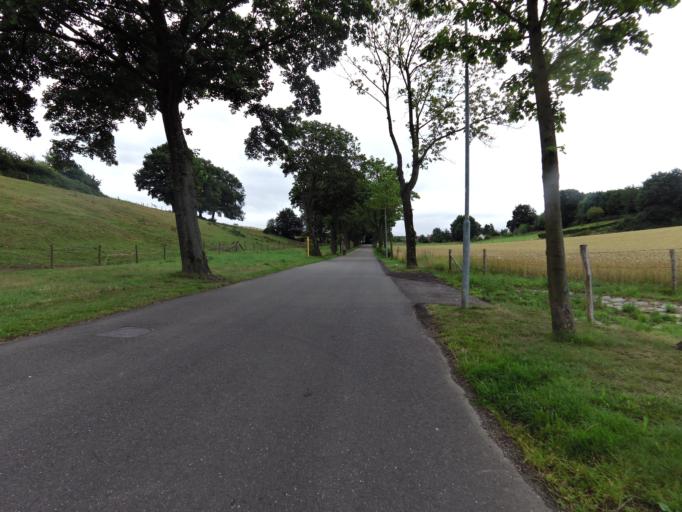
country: NL
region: Limburg
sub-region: Gemeente Nuth
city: Nuth
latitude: 50.9126
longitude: 5.8666
